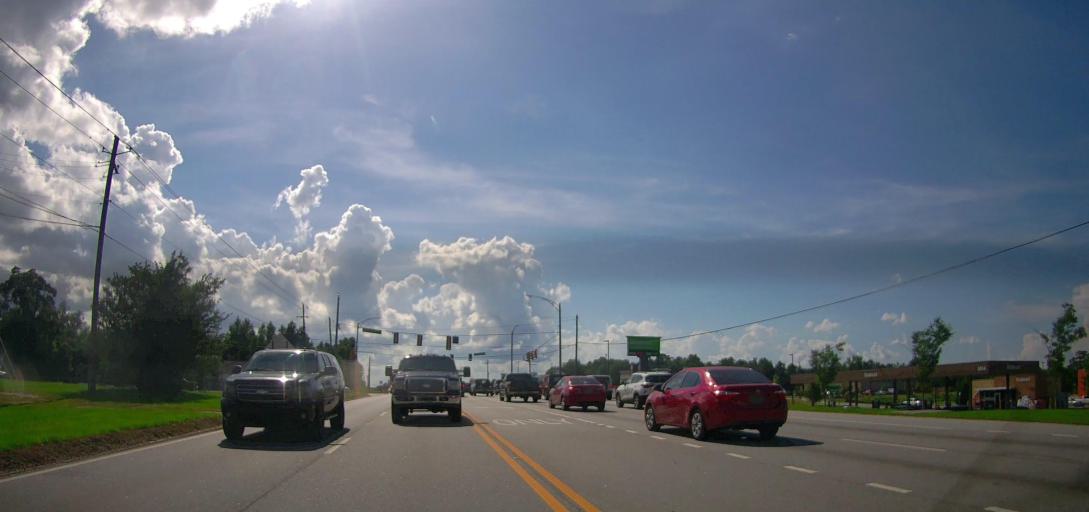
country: US
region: Alabama
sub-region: Russell County
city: Ladonia
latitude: 32.4692
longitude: -85.0835
